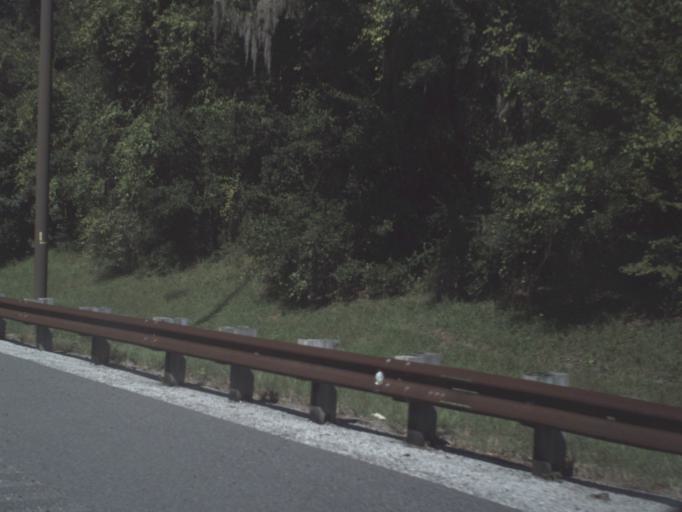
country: US
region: Florida
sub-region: Citrus County
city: Sugarmill Woods
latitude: 28.6453
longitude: -82.4904
